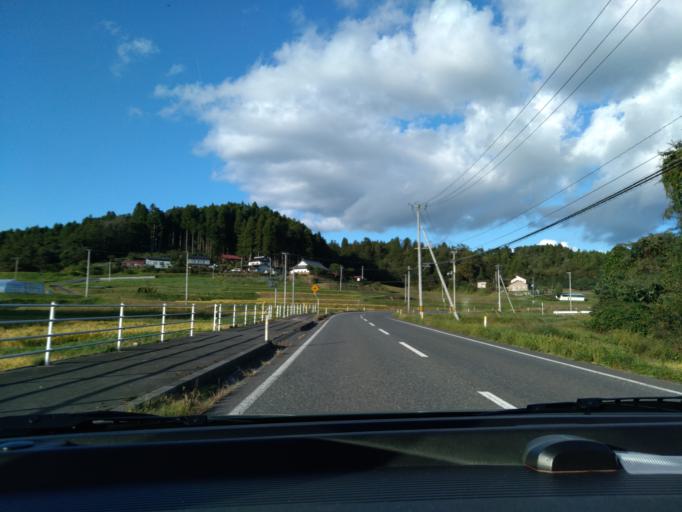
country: JP
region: Iwate
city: Ichinoseki
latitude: 38.8656
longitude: 141.1871
